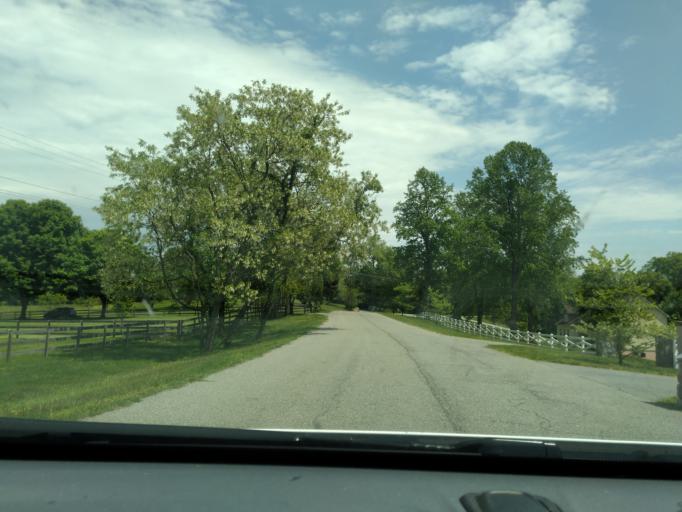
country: US
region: Maryland
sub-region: Prince George's County
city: Marlboro Meadows
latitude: 38.8529
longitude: -76.7119
